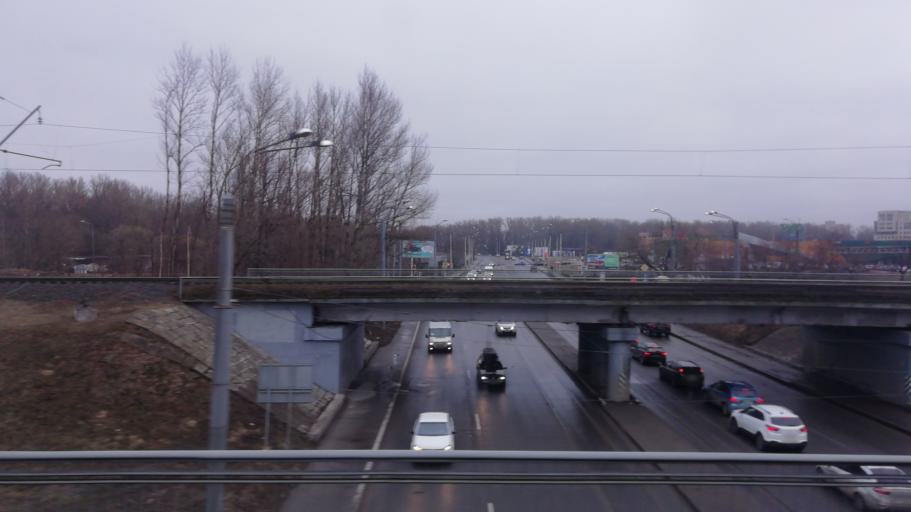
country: RU
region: St.-Petersburg
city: Kupchino
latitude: 59.8785
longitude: 30.3506
